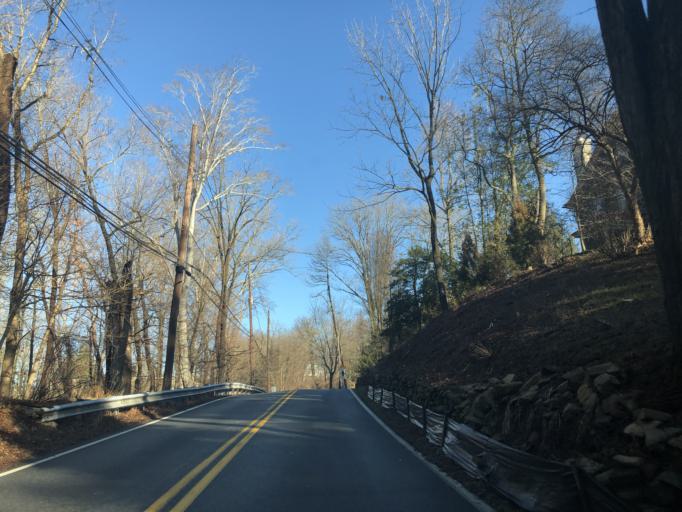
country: US
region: Pennsylvania
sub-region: Delaware County
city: Chester Heights
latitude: 39.9214
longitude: -75.4907
